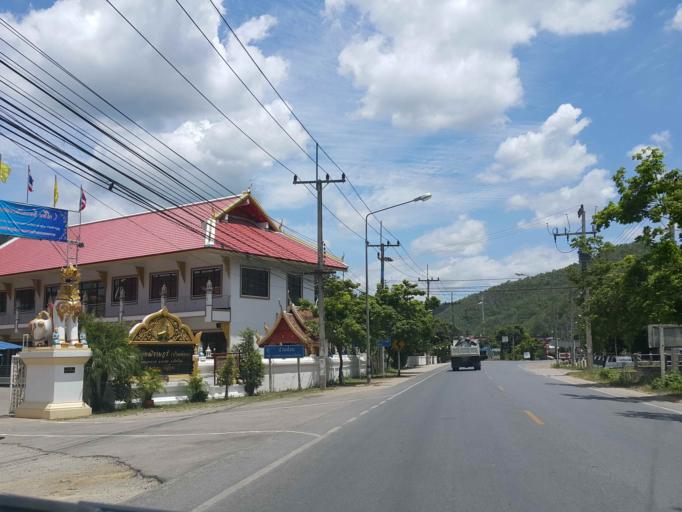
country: TH
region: Chiang Mai
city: Hang Dong
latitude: 18.7288
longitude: 98.9082
